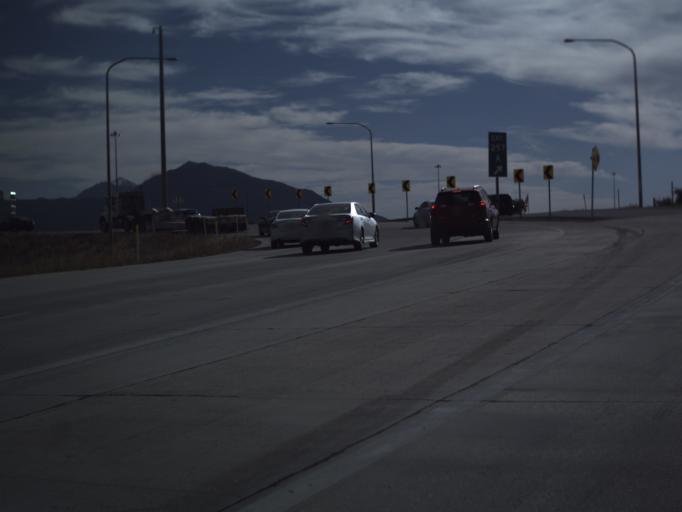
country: US
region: Utah
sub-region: Utah County
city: Spanish Fork
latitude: 40.1302
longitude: -111.6490
